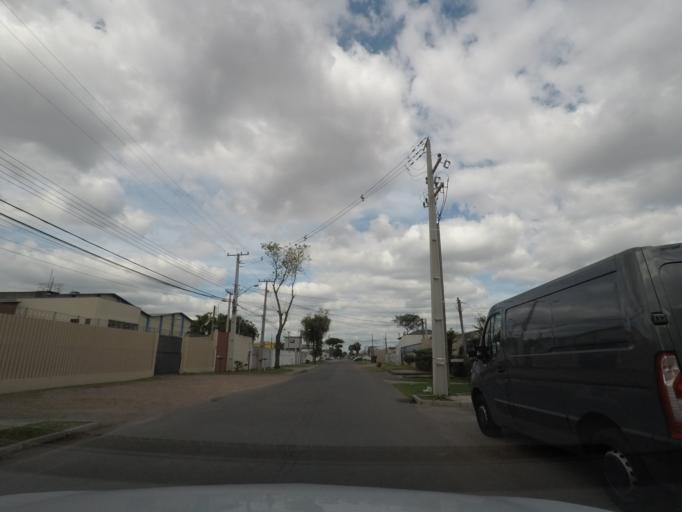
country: BR
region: Parana
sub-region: Sao Jose Dos Pinhais
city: Sao Jose dos Pinhais
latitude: -25.4874
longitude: -49.2391
